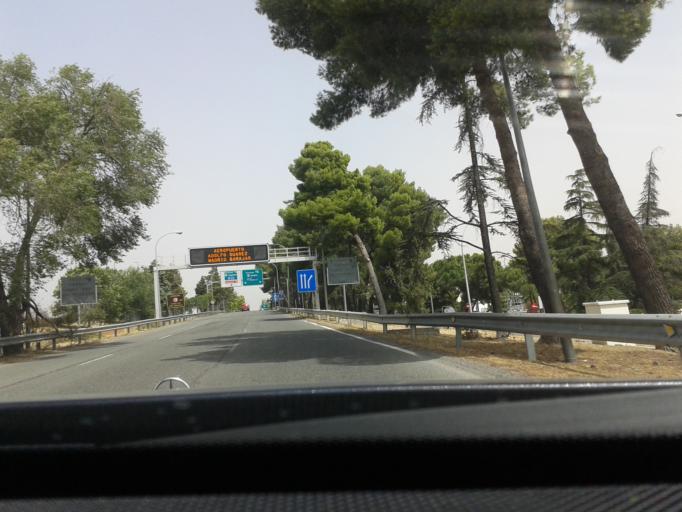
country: ES
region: Madrid
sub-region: Provincia de Madrid
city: Barajas de Madrid
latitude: 40.4638
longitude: -3.5744
